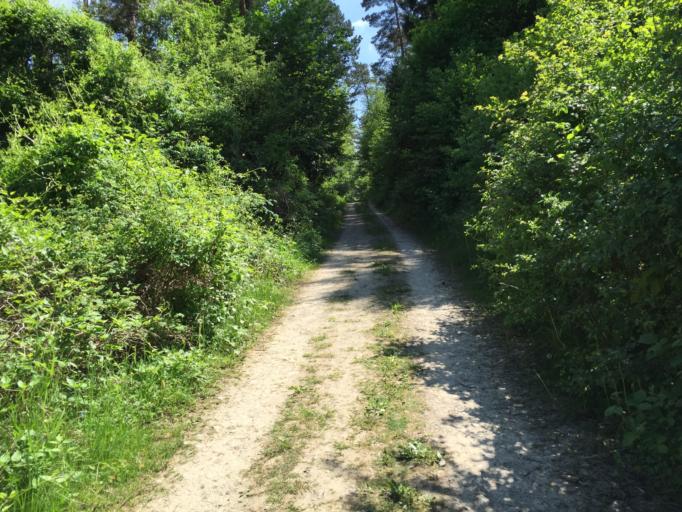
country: DE
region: Lower Saxony
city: Einbeck
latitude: 51.8254
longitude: 9.9076
